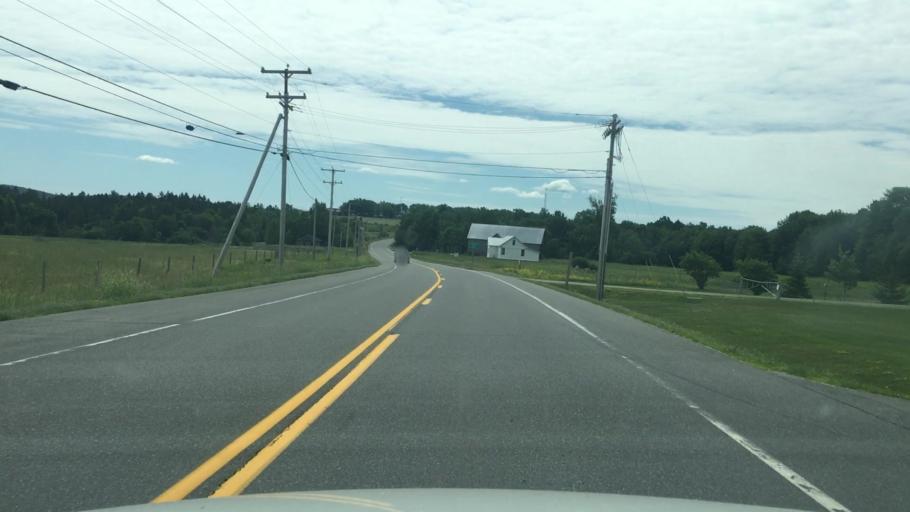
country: US
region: Maine
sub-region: Waldo County
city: Troy
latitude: 44.5508
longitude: -69.2681
